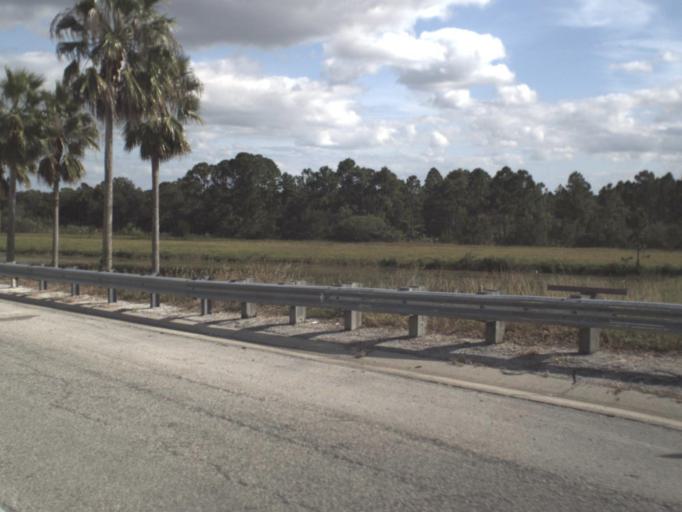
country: US
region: Florida
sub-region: Brevard County
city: Sharpes
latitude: 28.4116
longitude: -80.8183
